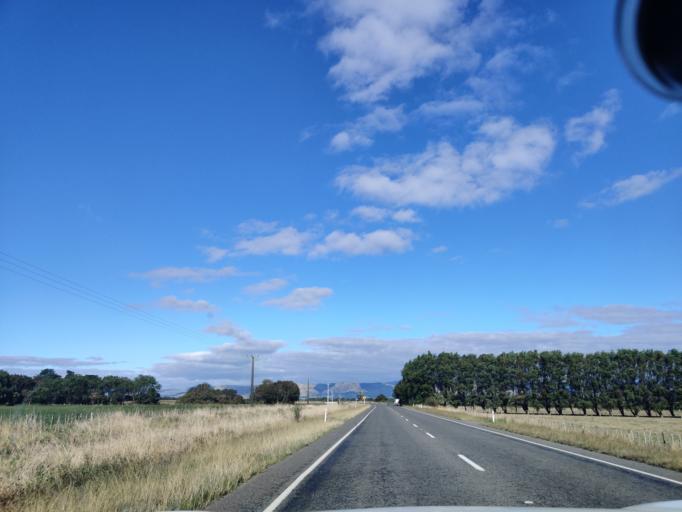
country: NZ
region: Manawatu-Wanganui
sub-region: Horowhenua District
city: Foxton
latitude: -40.4239
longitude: 175.4505
